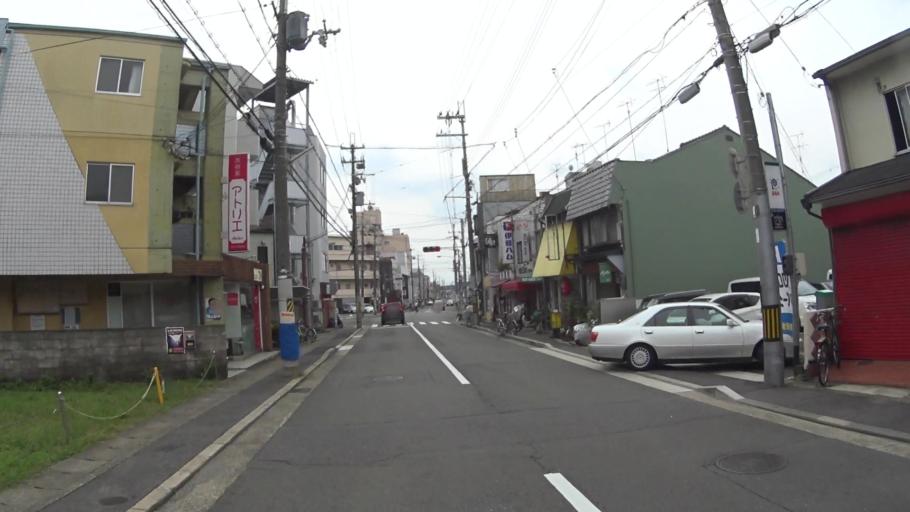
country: JP
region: Kyoto
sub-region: Kyoto-shi
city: Kamigyo-ku
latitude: 35.0465
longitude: 135.7866
